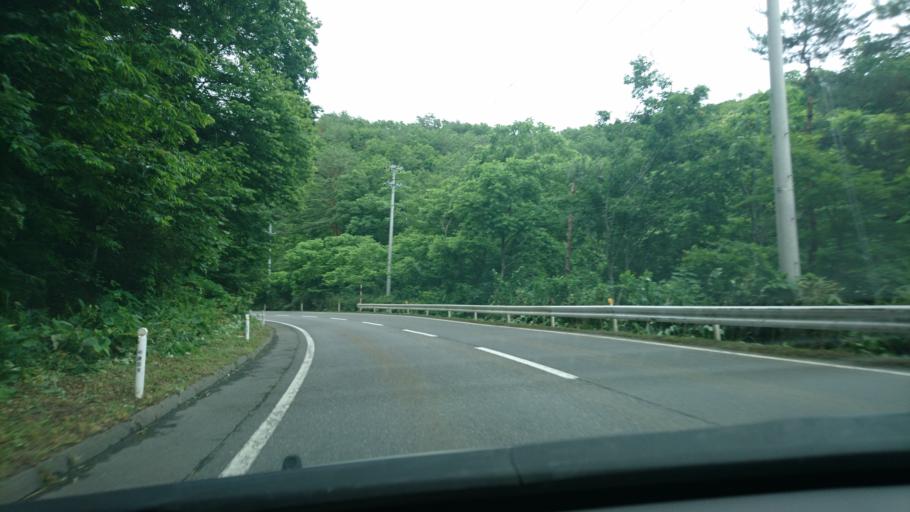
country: JP
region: Iwate
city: Miyako
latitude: 39.9673
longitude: 141.8596
